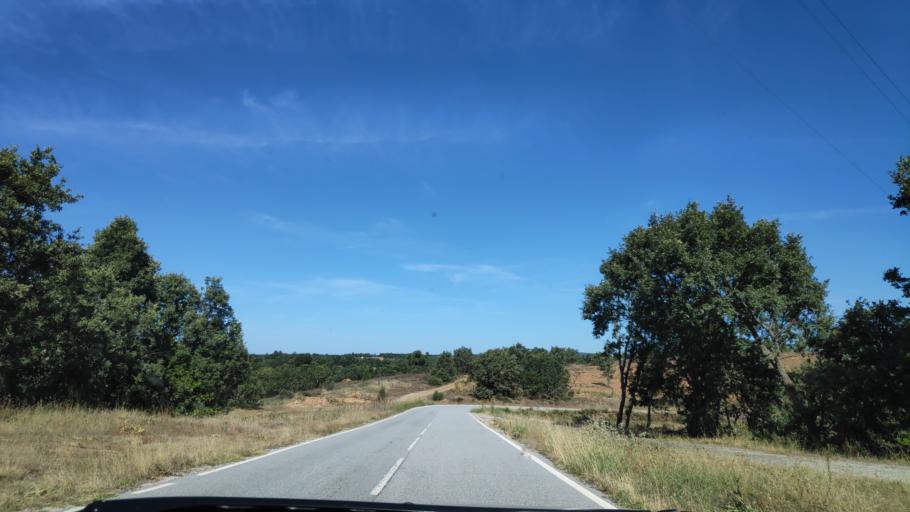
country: ES
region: Castille and Leon
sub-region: Provincia de Zamora
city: Alcanices
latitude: 41.6257
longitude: -6.3485
